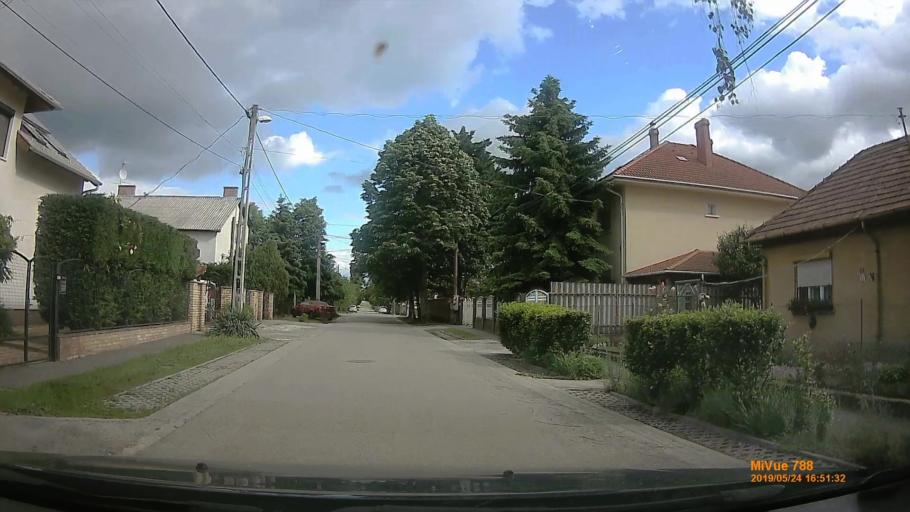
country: HU
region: Pest
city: Csomor
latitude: 47.5098
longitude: 19.2211
